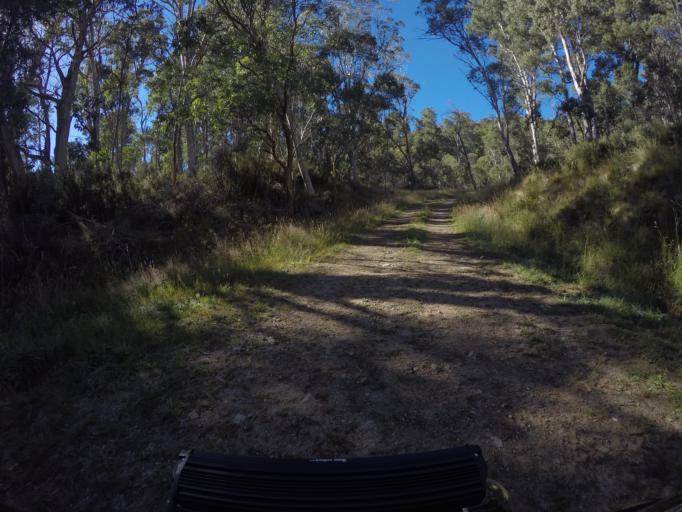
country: AU
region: New South Wales
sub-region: Snowy River
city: Jindabyne
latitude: -36.0476
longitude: 148.2948
